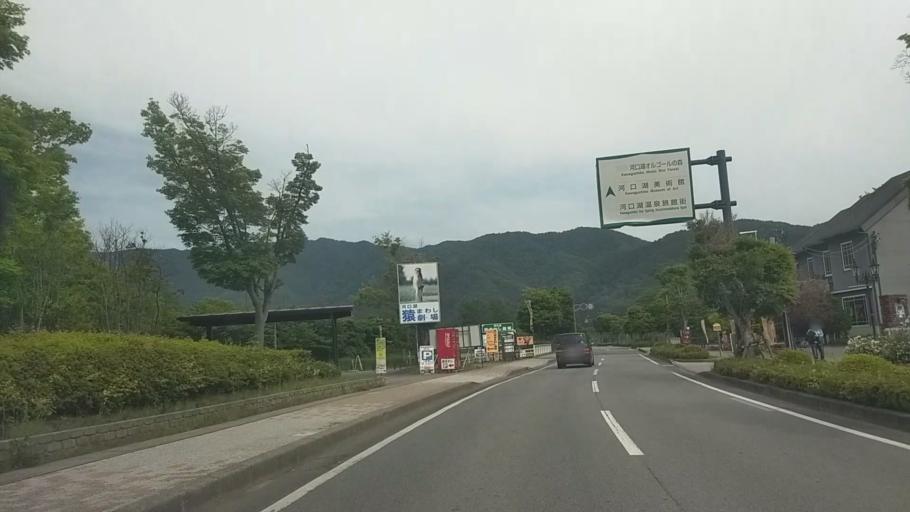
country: JP
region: Yamanashi
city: Fujikawaguchiko
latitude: 35.5248
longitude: 138.7650
